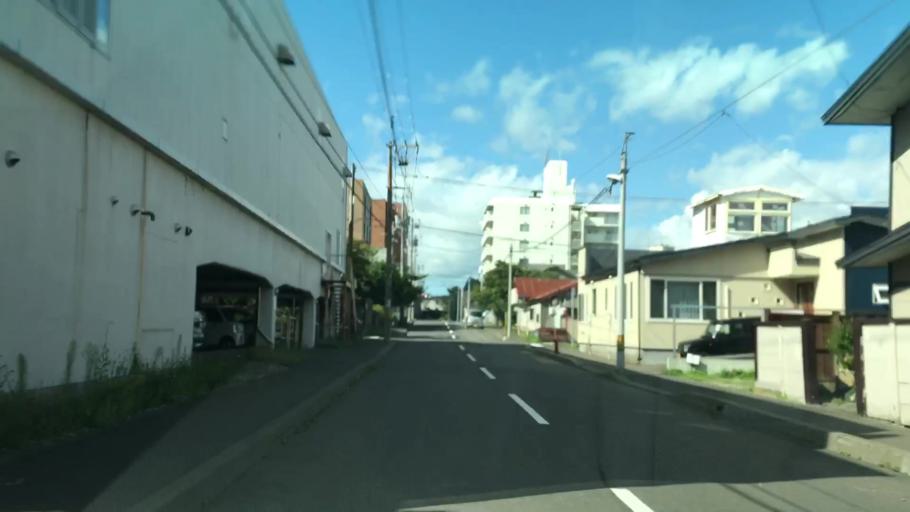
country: JP
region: Hokkaido
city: Muroran
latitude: 42.3143
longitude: 140.9712
